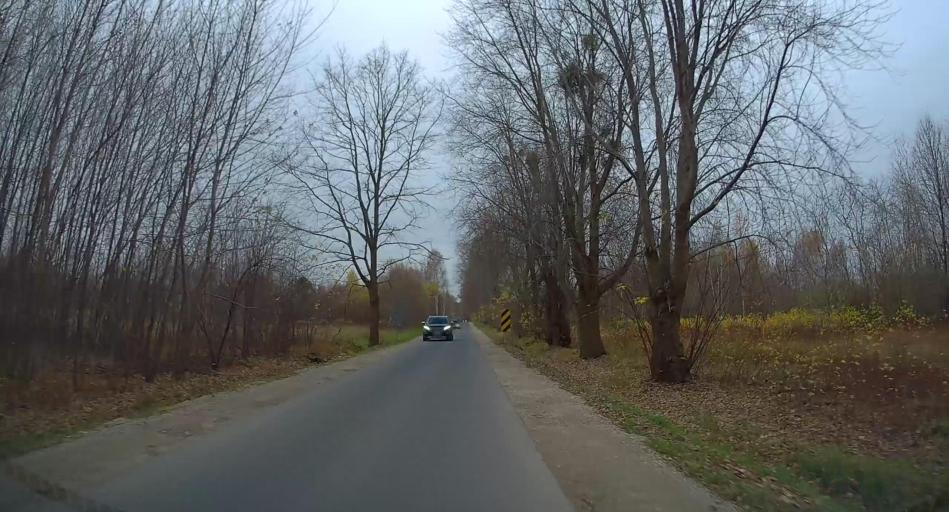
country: PL
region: Lodz Voivodeship
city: Zabia Wola
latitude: 52.0155
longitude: 20.6555
